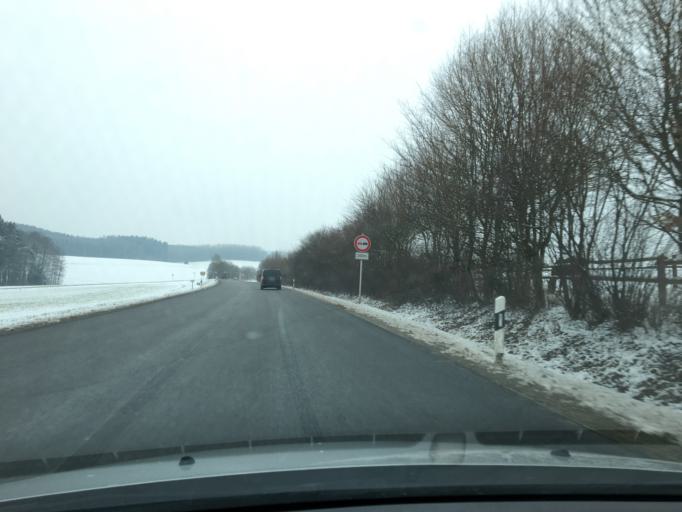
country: DE
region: Bavaria
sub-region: Upper Bavaria
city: Egglkofen
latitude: 48.4162
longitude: 12.4239
